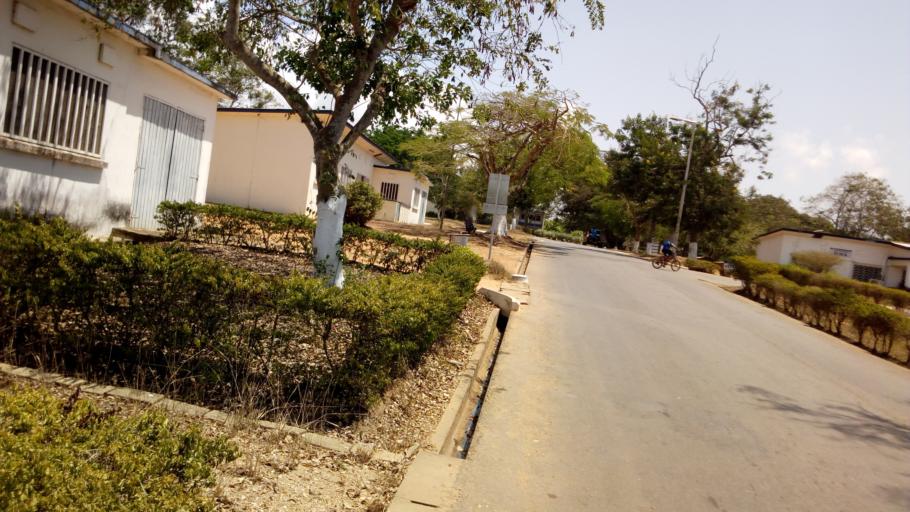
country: GH
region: Central
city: Cape Coast
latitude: 5.1057
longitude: -1.2833
